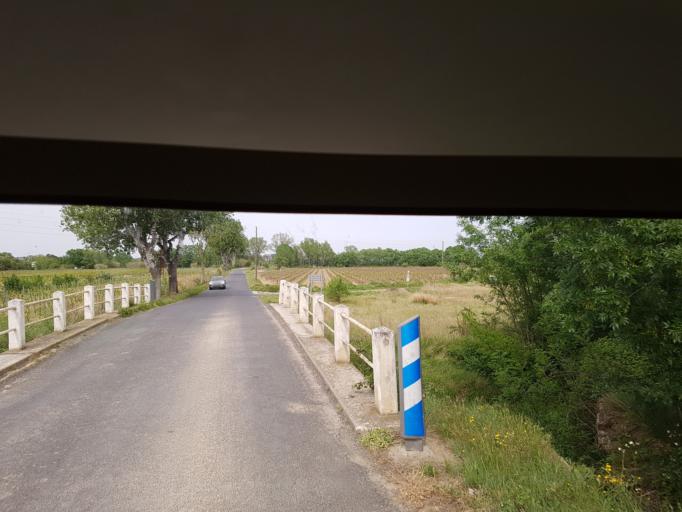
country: FR
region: Languedoc-Roussillon
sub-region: Departement de l'Aude
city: Fleury
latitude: 43.2417
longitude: 3.1492
